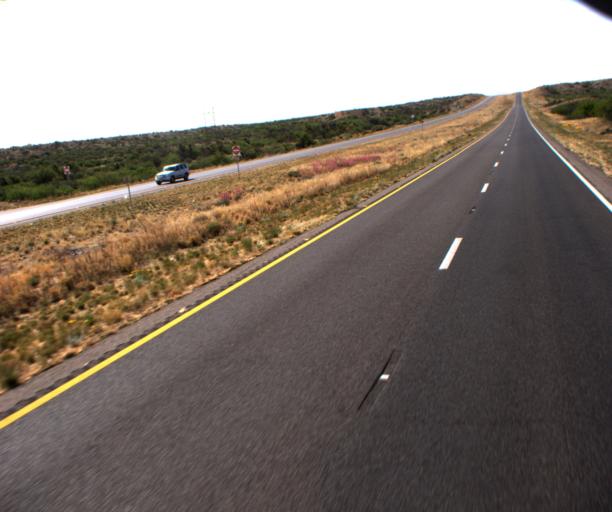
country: US
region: Arizona
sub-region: Graham County
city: Swift Trail Junction
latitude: 32.5873
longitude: -109.6837
